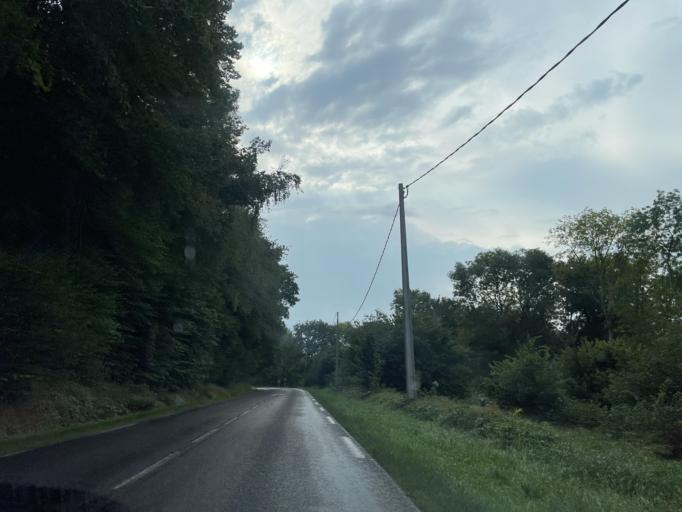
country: FR
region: Haute-Normandie
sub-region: Departement de la Seine-Maritime
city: Neufchatel-en-Bray
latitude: 49.7574
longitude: 1.4256
